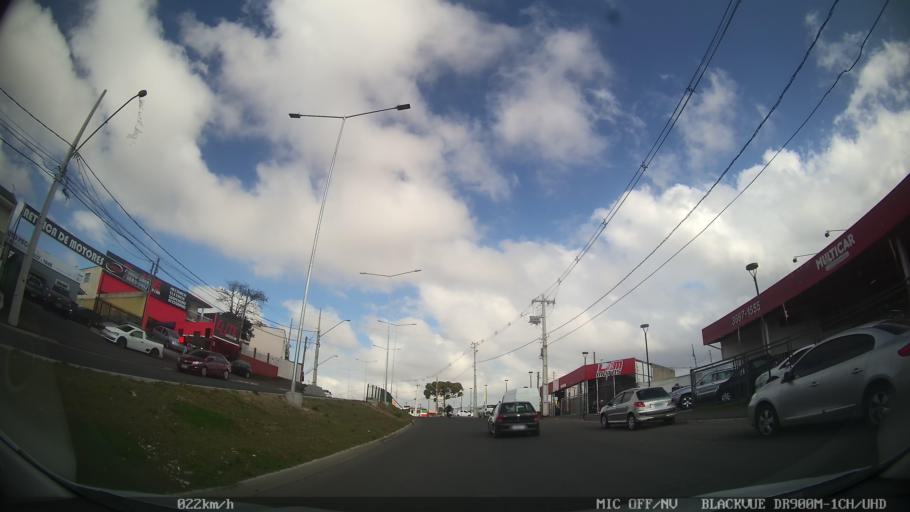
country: BR
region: Parana
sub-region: Pinhais
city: Pinhais
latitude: -25.3743
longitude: -49.1866
